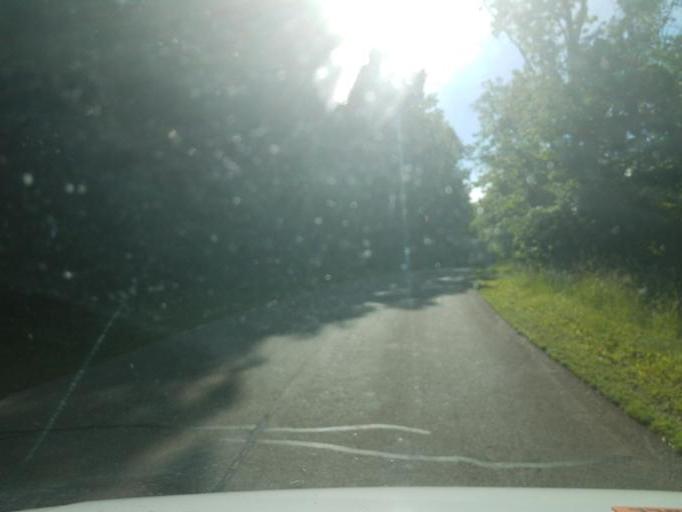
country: US
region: Wisconsin
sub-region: Sauk County
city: Reedsburg
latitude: 43.5497
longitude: -90.1114
